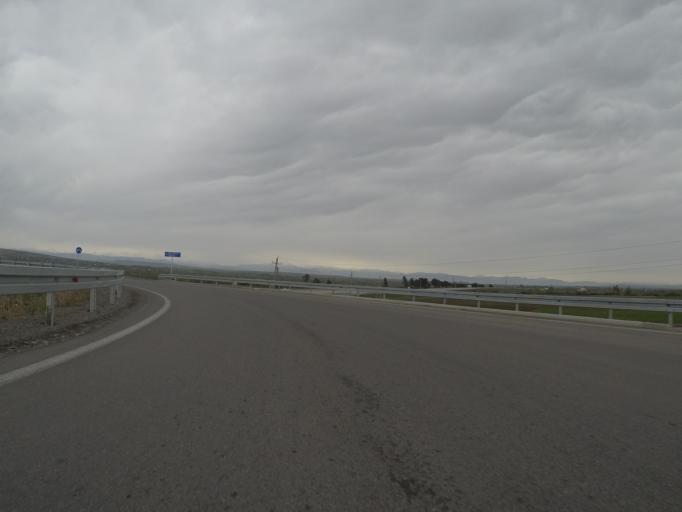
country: GE
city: Agara
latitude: 42.0261
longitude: 43.7689
